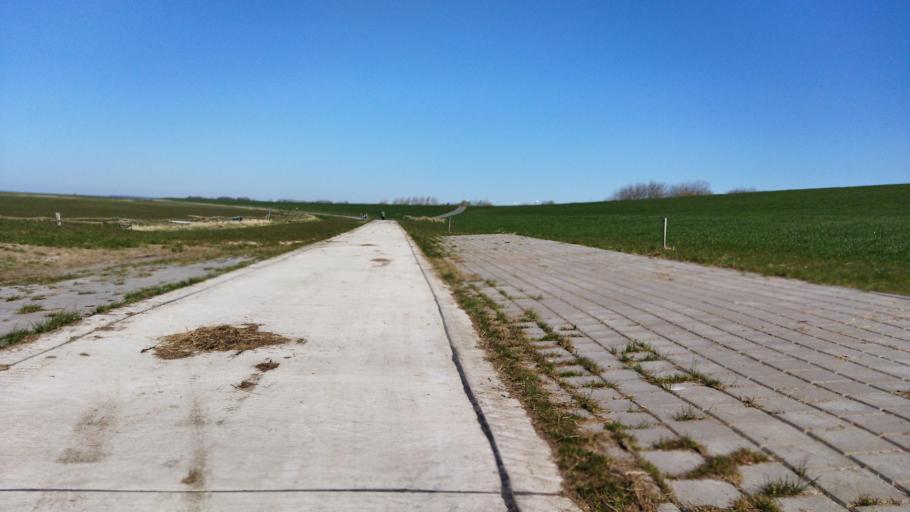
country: DE
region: Lower Saxony
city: Padingbuttel
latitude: 53.7425
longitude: 8.5232
